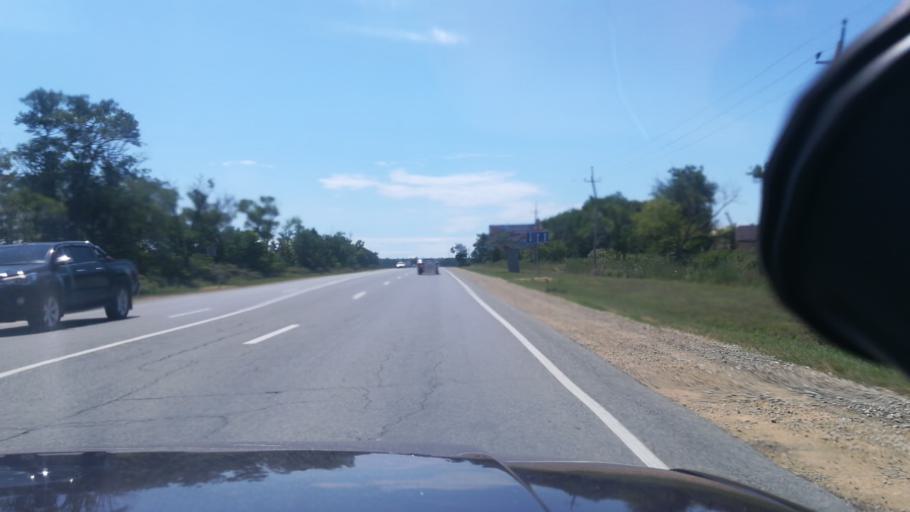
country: RU
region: Krasnodarskiy
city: Tsibanobalka
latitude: 44.9873
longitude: 37.3218
